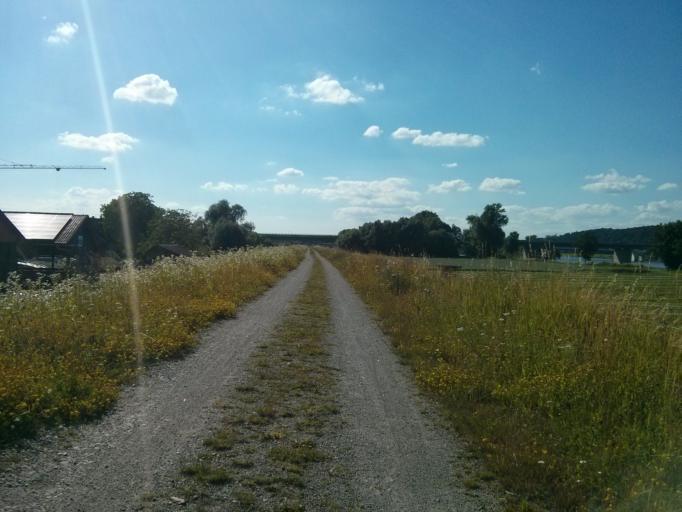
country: DE
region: Bavaria
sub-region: Lower Bavaria
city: Deggendorf
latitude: 48.8247
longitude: 12.9514
